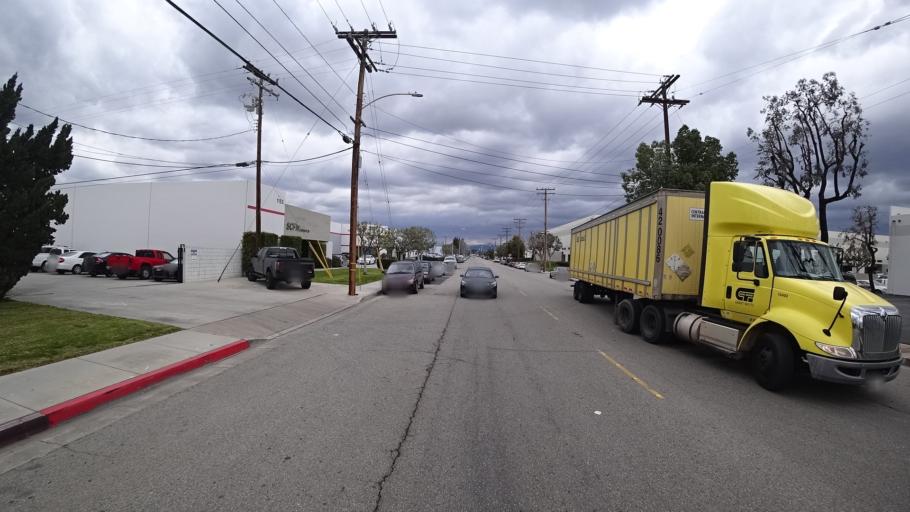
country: US
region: California
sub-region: Orange County
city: Placentia
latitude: 33.8511
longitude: -117.8641
